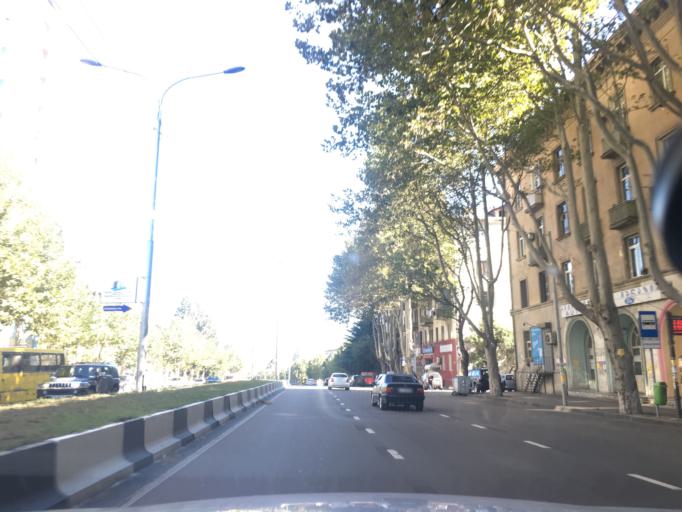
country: GE
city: Zahesi
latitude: 41.7723
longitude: 44.7938
